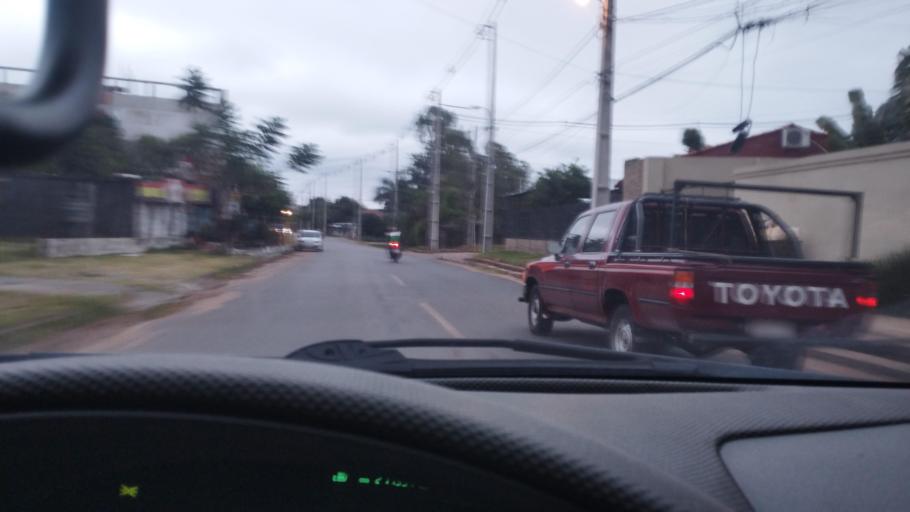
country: PY
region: Central
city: Fernando de la Mora
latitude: -25.2912
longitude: -57.5125
